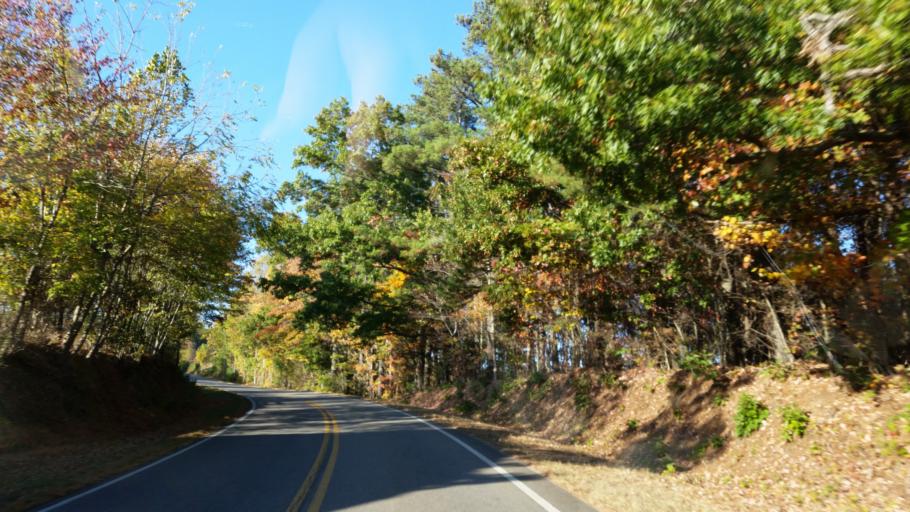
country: US
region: Georgia
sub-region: Gilmer County
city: Ellijay
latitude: 34.5851
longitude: -84.4571
